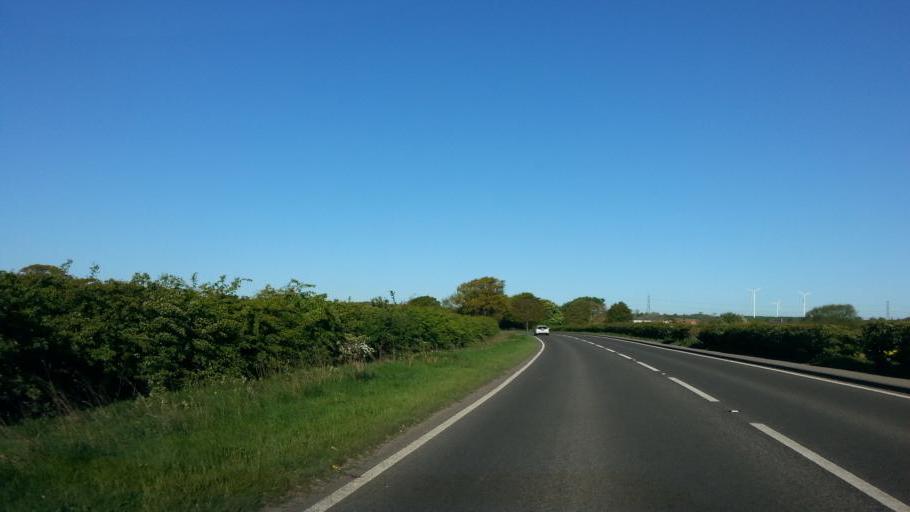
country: GB
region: England
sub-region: Nottinghamshire
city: Newark on Trent
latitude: 53.1053
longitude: -0.8281
